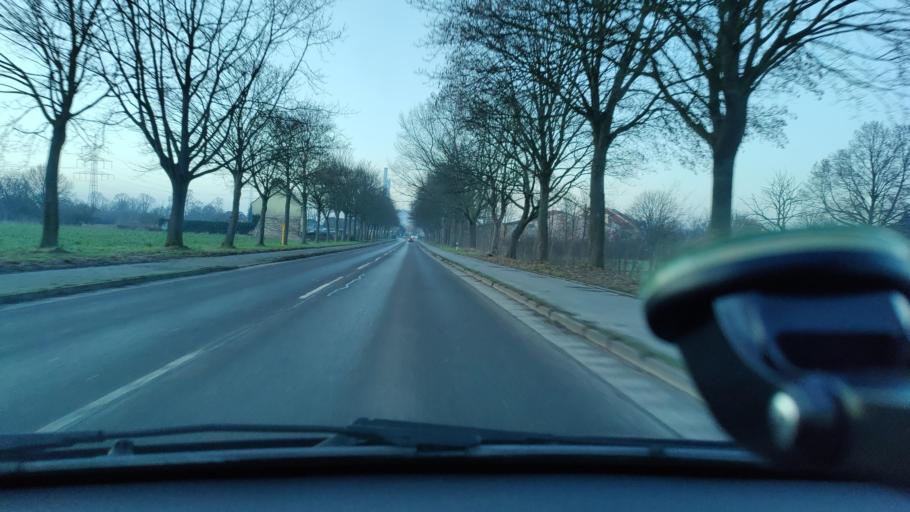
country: DE
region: North Rhine-Westphalia
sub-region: Regierungsbezirk Dusseldorf
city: Dinslaken
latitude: 51.5617
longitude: 6.7057
